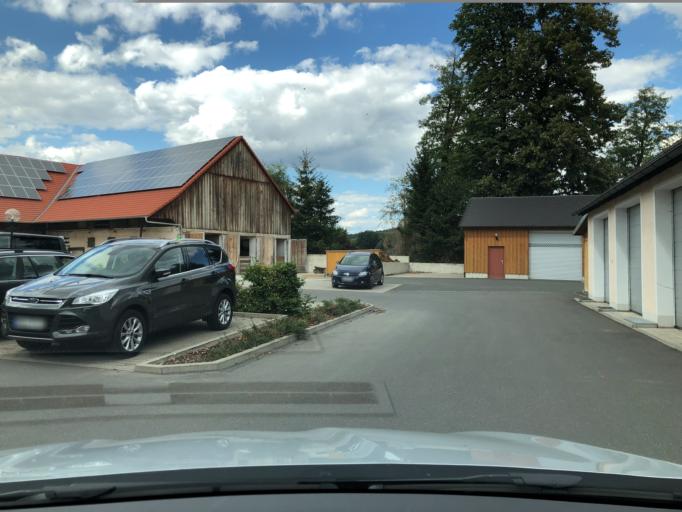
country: DE
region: Bavaria
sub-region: Upper Palatinate
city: Poppenricht
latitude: 49.4912
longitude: 11.8207
